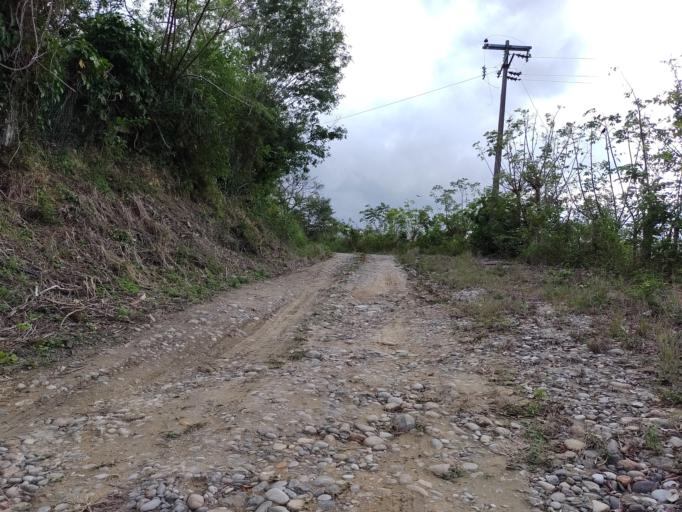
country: MX
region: Veracruz
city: Papantla de Olarte
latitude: 20.4499
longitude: -97.3084
